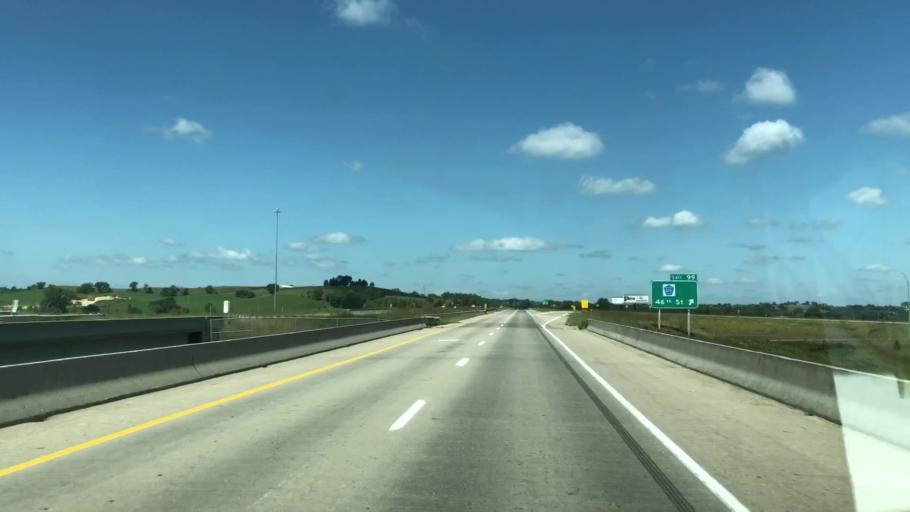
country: US
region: Iowa
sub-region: Woodbury County
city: Sioux City
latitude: 42.5457
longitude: -96.3404
